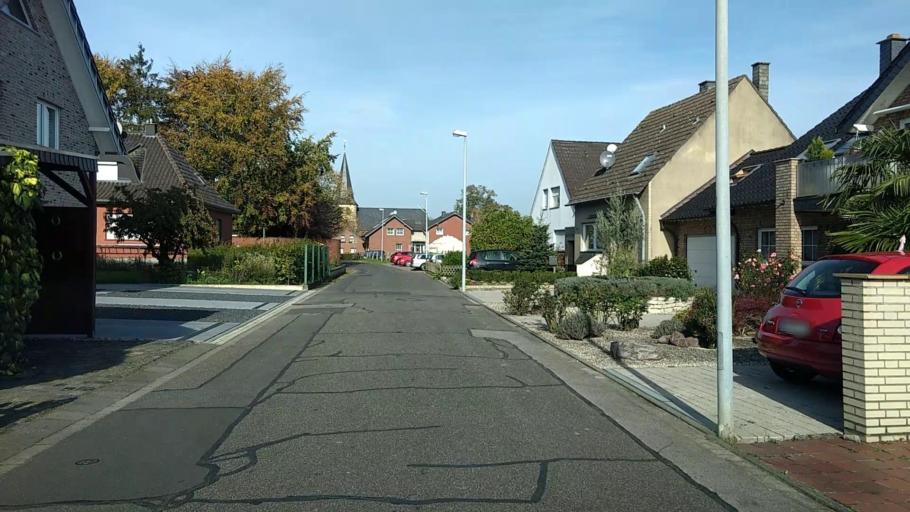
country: DE
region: North Rhine-Westphalia
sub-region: Regierungsbezirk Koln
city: Bergheim
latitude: 50.9112
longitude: 6.6402
